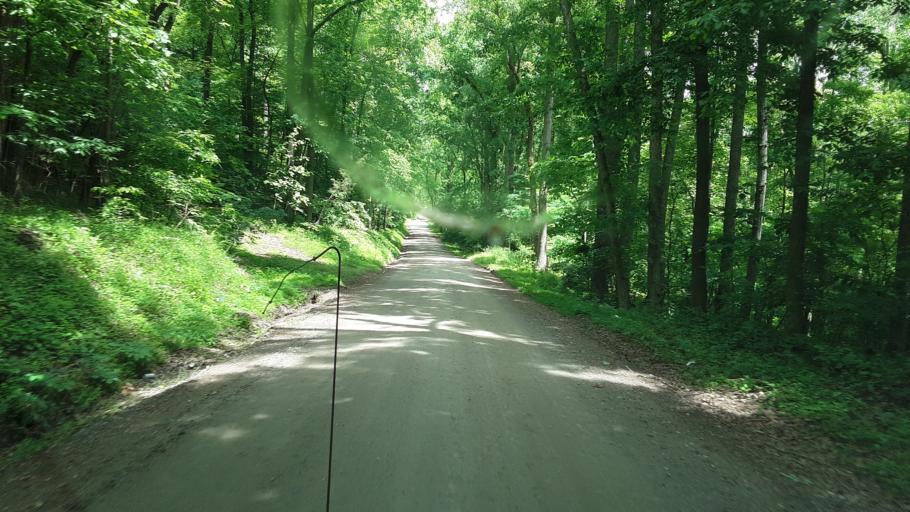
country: US
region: Virginia
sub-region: Pittsylvania County
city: Chatham
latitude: 36.8449
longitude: -79.4306
